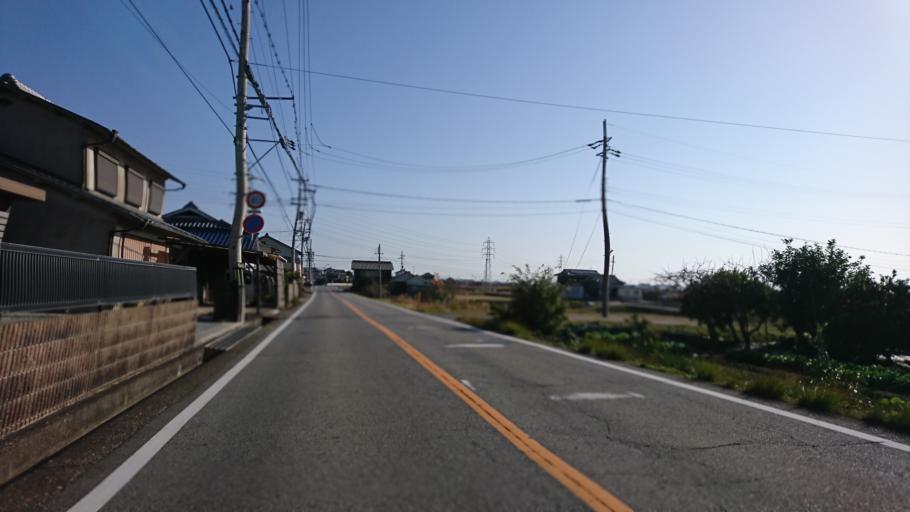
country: JP
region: Hyogo
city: Kakogawacho-honmachi
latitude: 34.7625
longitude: 134.8939
